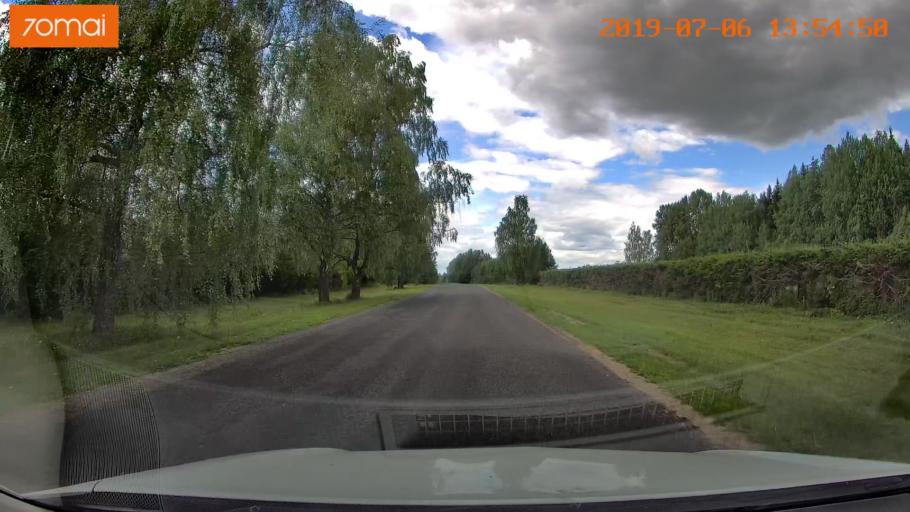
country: BY
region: Minsk
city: Ivyanyets
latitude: 53.7497
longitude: 26.8159
